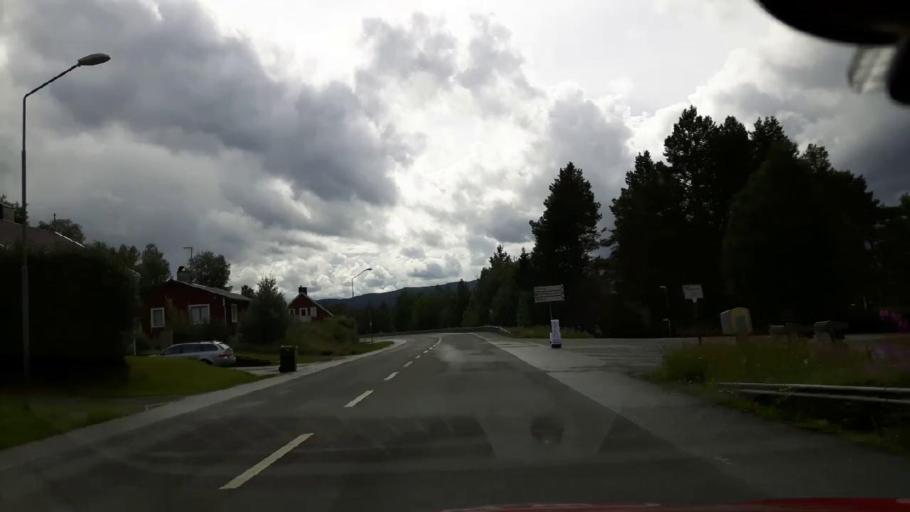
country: NO
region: Nord-Trondelag
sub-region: Lierne
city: Sandvika
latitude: 64.4903
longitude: 14.1510
